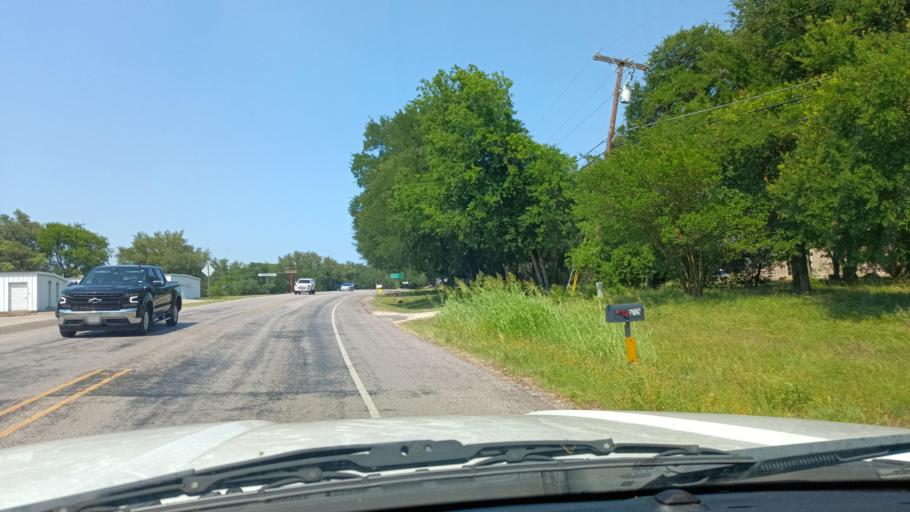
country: US
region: Texas
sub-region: Bell County
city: Belton
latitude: 31.1022
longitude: -97.5152
